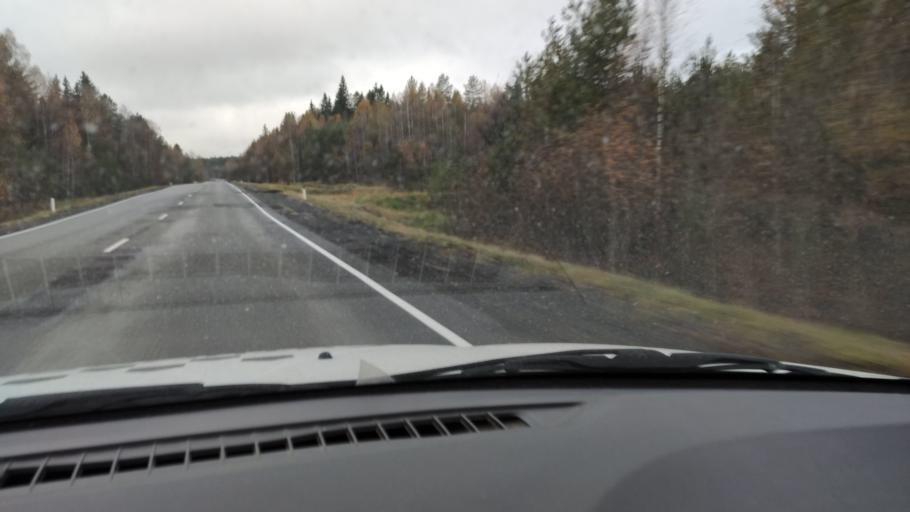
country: RU
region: Kirov
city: Dubrovka
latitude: 58.9062
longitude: 51.2618
